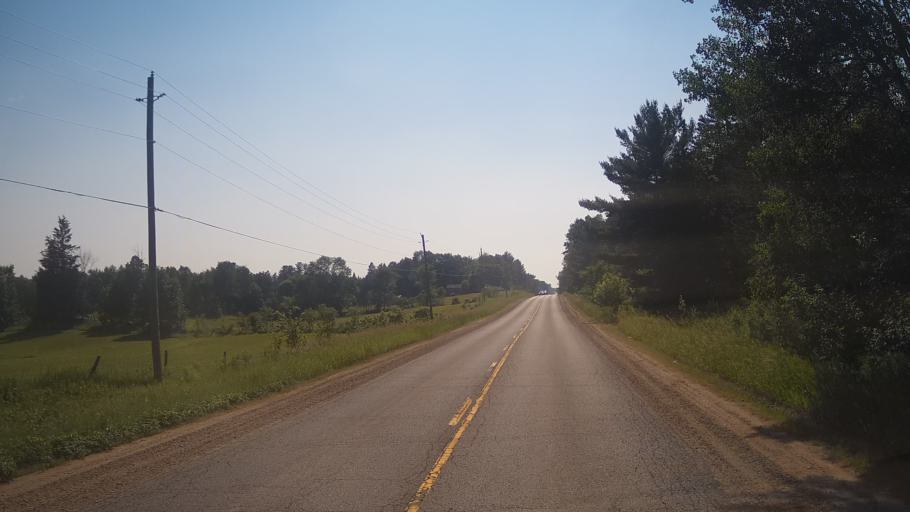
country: CA
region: Ontario
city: Pembroke
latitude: 45.6097
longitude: -77.2057
